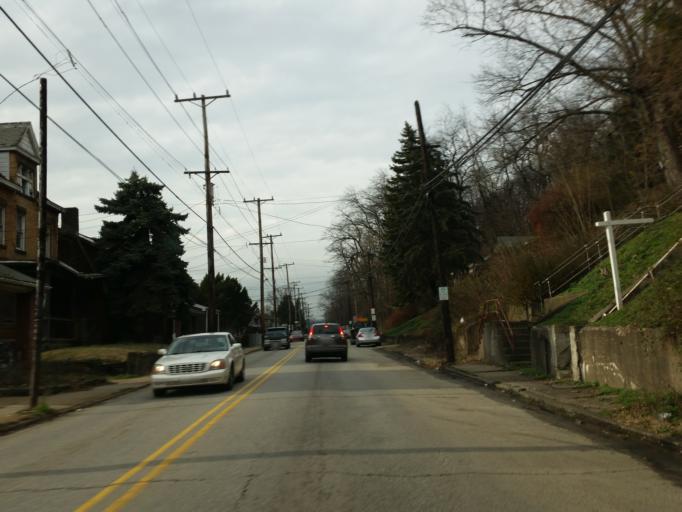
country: US
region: Pennsylvania
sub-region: Allegheny County
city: Rankin
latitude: 40.4175
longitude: -79.8792
